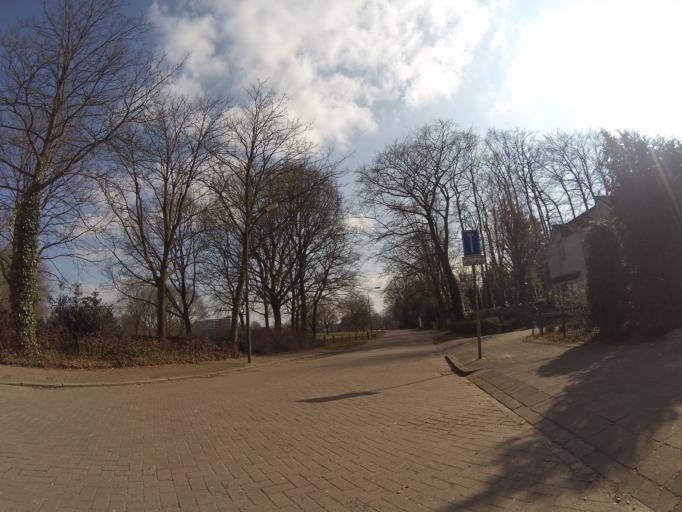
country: NL
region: Utrecht
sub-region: Gemeente Soest
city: Soest
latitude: 52.1812
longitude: 5.2914
